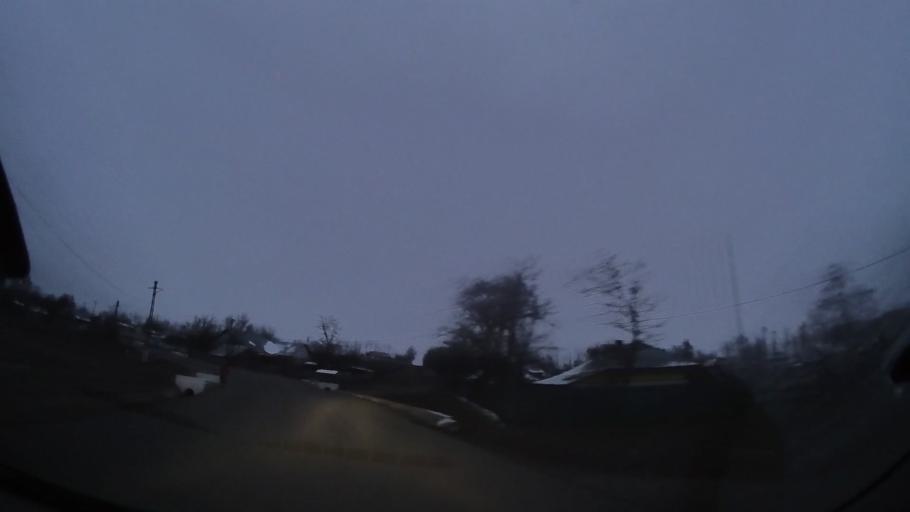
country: RO
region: Vaslui
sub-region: Comuna Dimitrie Cantemir
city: Dimitrie Cantemir
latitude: 46.4625
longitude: 28.0314
